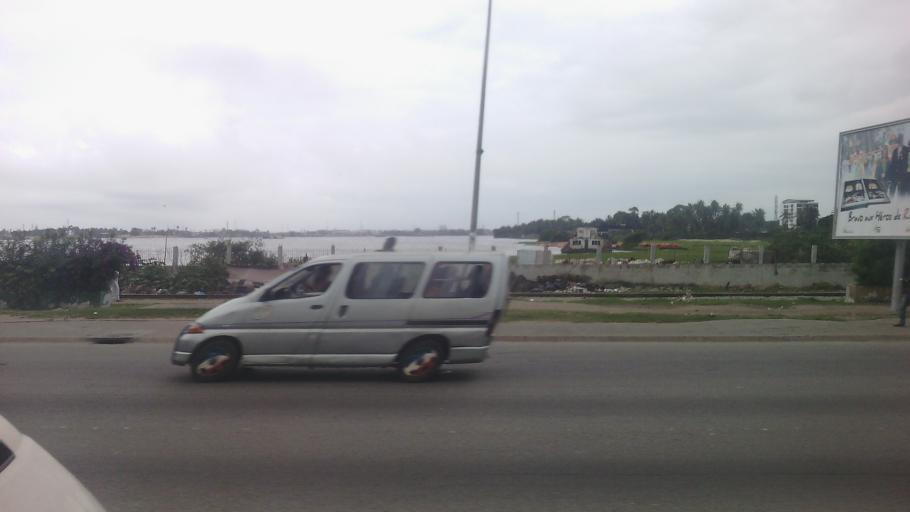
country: CI
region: Lagunes
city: Abidjan
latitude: 5.2738
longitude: -3.9646
